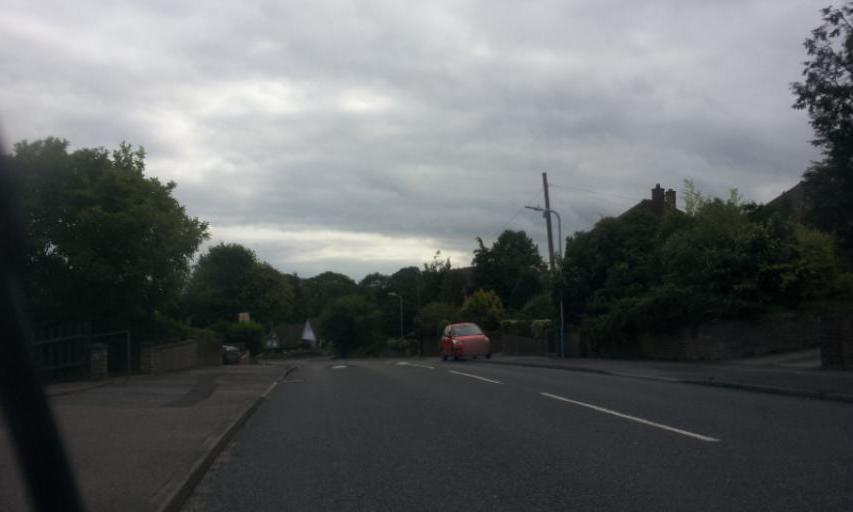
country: GB
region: England
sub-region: Kent
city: Tonbridge
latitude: 51.2101
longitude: 0.2932
